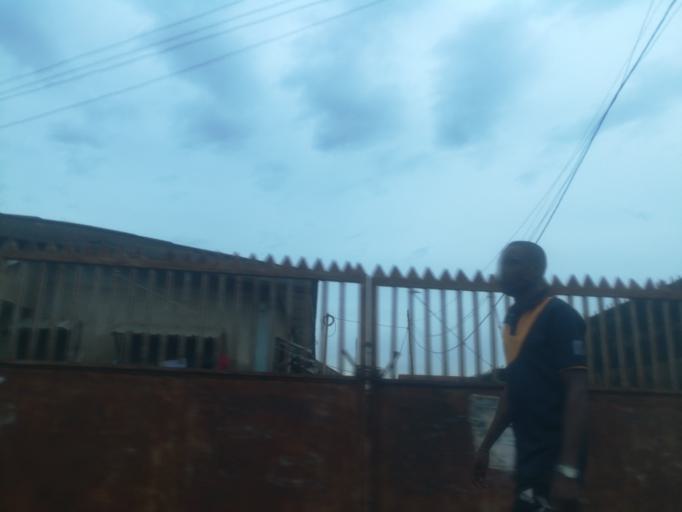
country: NG
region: Oyo
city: Ibadan
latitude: 7.4025
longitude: 3.9674
